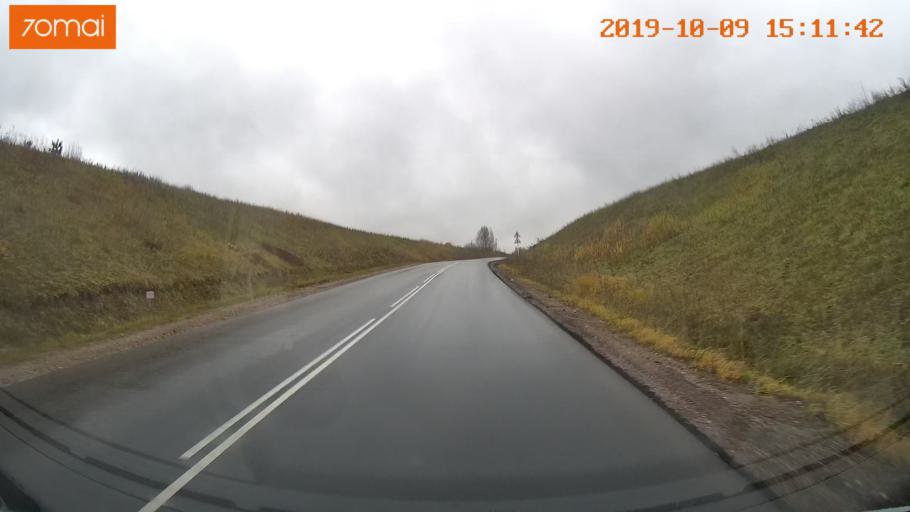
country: RU
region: Kostroma
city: Susanino
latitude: 58.1612
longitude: 41.6284
